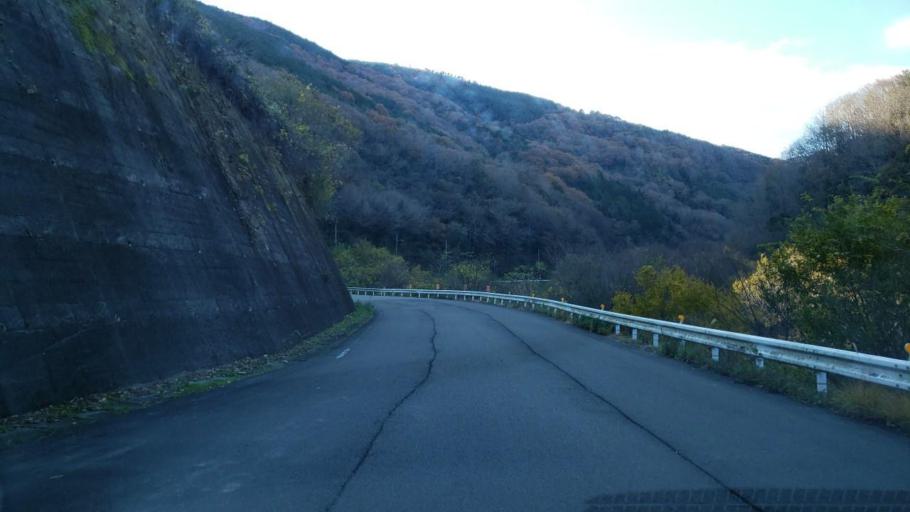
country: JP
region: Tokushima
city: Wakimachi
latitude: 34.0757
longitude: 134.0795
